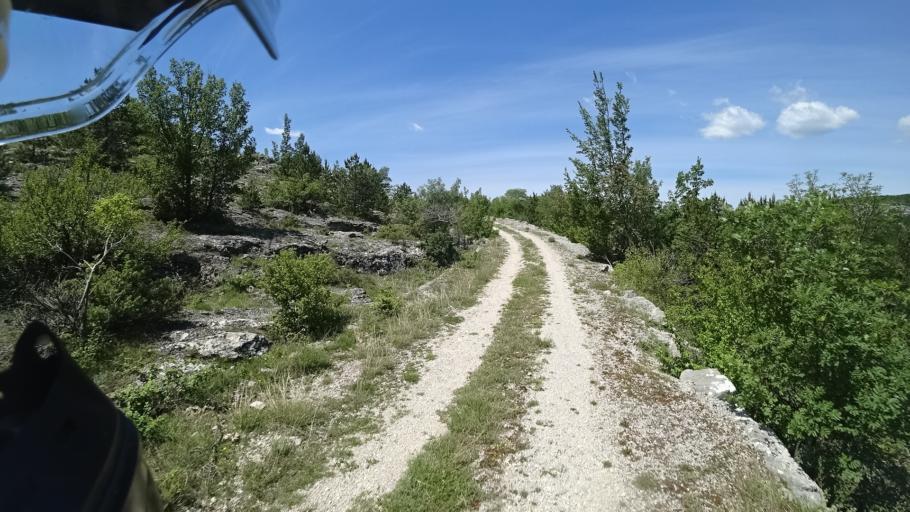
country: HR
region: Sibensko-Kniniska
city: Knin
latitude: 44.0327
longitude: 16.2511
